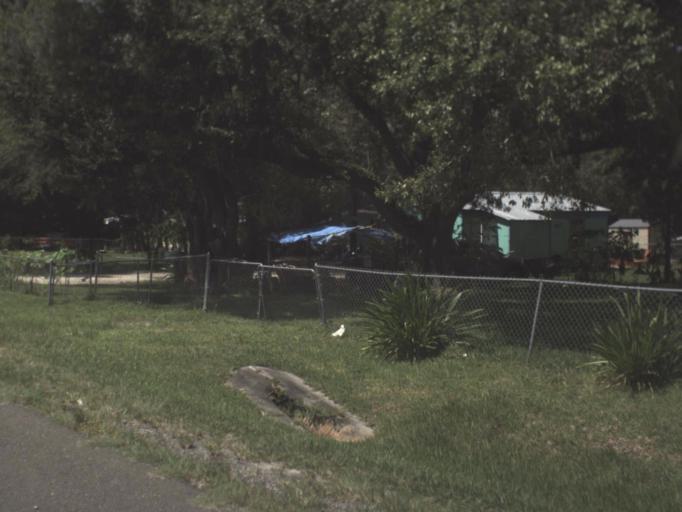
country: US
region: Florida
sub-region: DeSoto County
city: Southeast Arcadia
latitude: 27.1849
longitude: -81.8706
